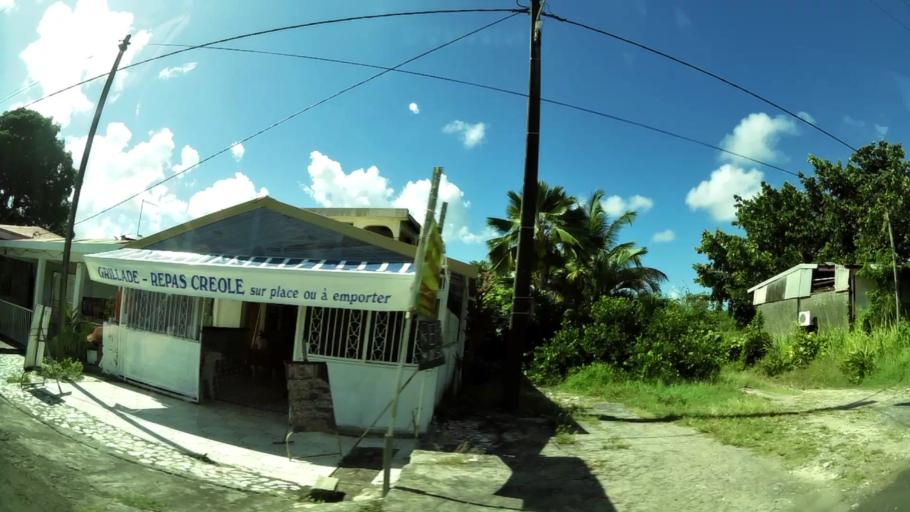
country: GP
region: Guadeloupe
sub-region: Guadeloupe
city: Petit-Canal
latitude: 16.3792
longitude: -61.4554
